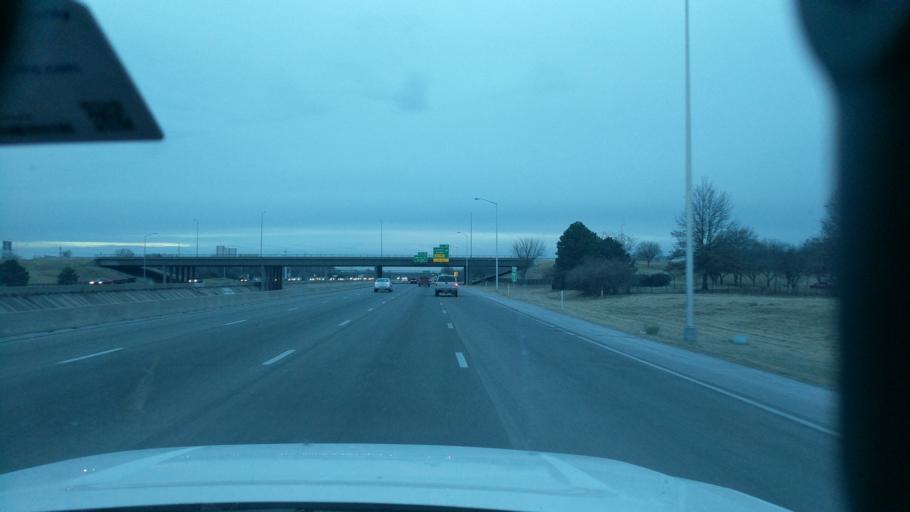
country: US
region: Kansas
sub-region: Sedgwick County
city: Wichita
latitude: 37.6736
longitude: -97.3127
